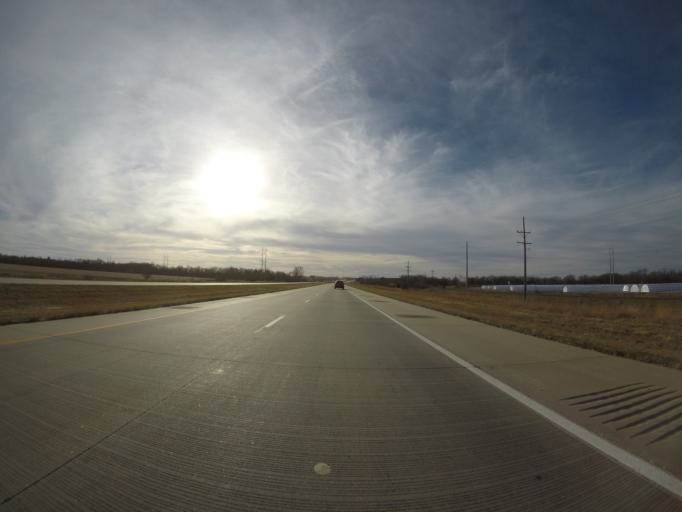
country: US
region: Kansas
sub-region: Franklin County
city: Ottawa
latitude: 38.5795
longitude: -95.2559
